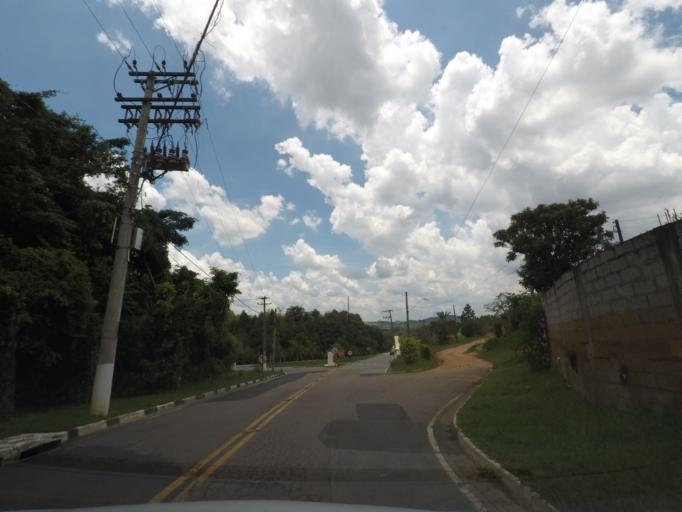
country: BR
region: Sao Paulo
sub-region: Vinhedo
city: Vinhedo
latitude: -23.0506
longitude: -46.9629
